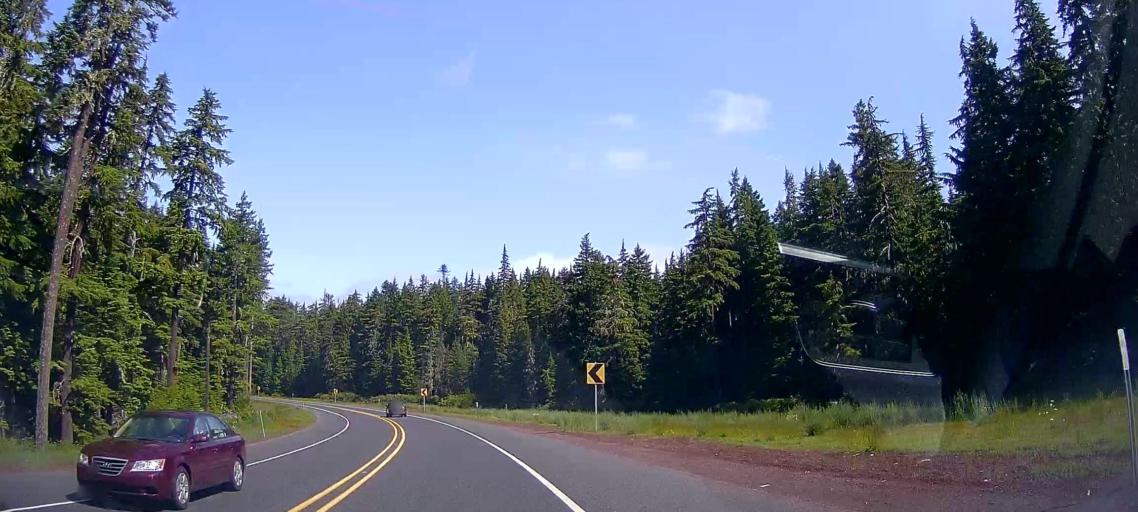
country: US
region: Oregon
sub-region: Clackamas County
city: Mount Hood Village
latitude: 45.1870
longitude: -121.6772
